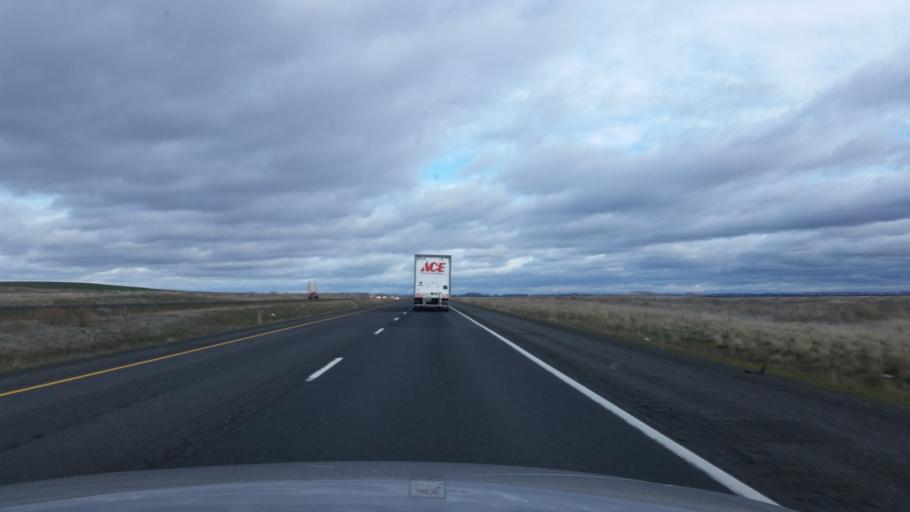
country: US
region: Washington
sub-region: Spokane County
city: Medical Lake
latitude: 47.3166
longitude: -117.9543
